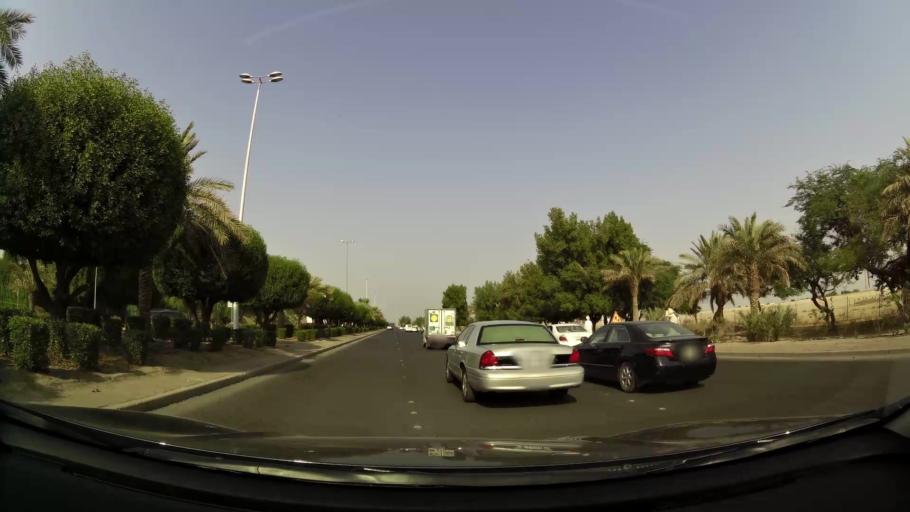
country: KW
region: Muhafazat al Jahra'
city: Al Jahra'
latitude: 29.3351
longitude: 47.7089
